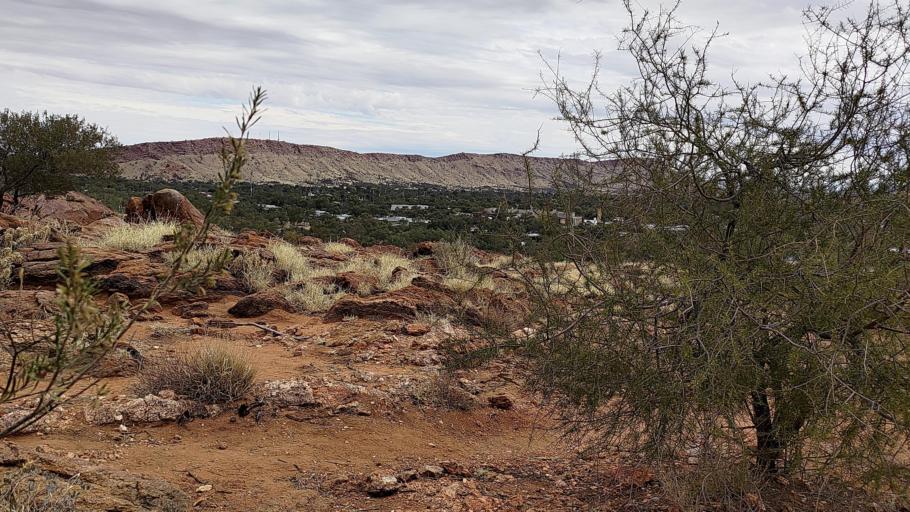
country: AU
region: Northern Territory
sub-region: Alice Springs
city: Alice Springs
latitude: -23.7049
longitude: 133.8851
